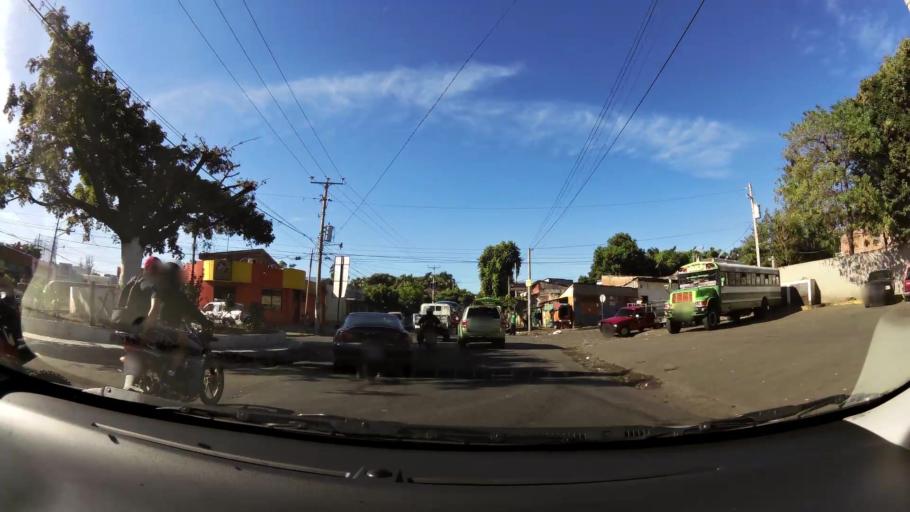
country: SV
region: Santa Ana
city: Santa Ana
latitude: 13.9888
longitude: -89.5653
